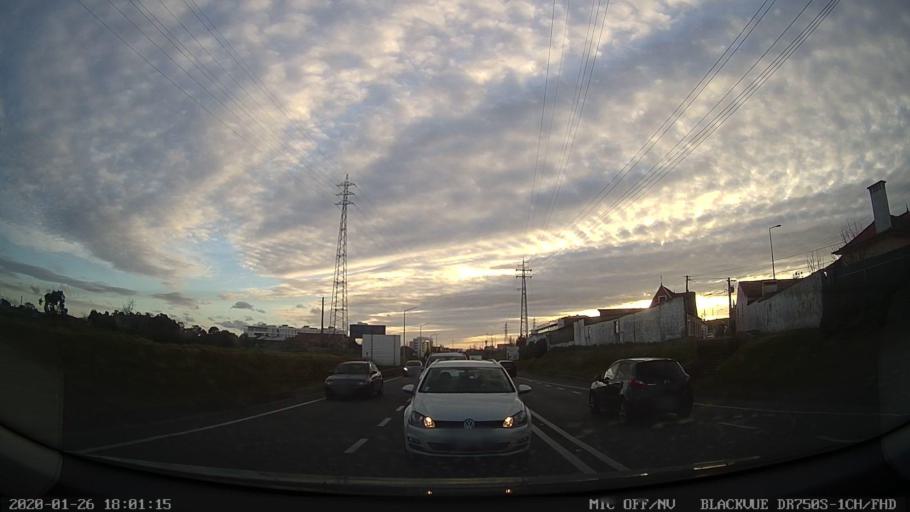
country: PT
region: Aveiro
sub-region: Aveiro
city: Aveiro
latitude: 40.6395
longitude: -8.6326
